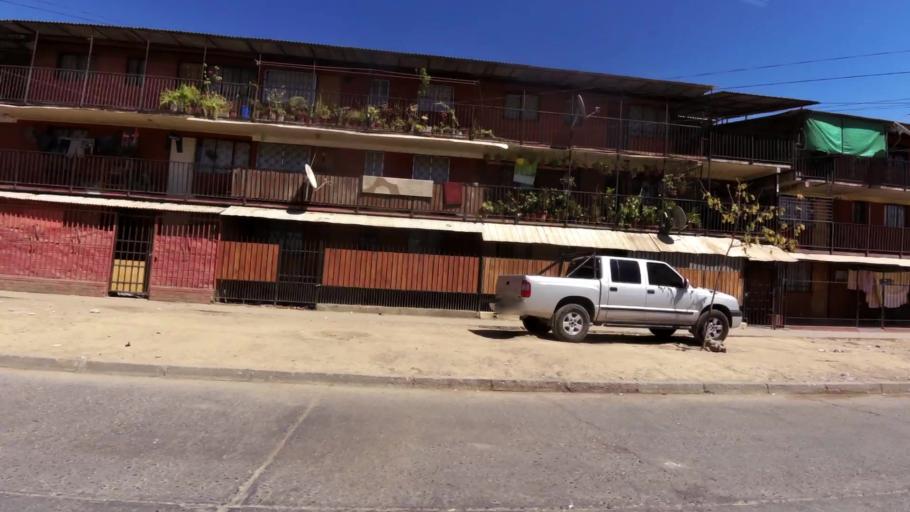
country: CL
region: O'Higgins
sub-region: Provincia de Cachapoal
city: Rancagua
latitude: -34.1648
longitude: -70.7199
